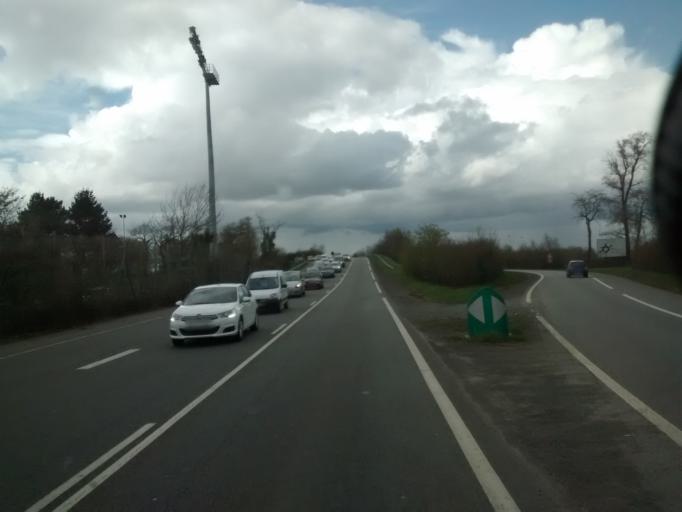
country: FR
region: Brittany
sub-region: Departement d'Ille-et-Vilaine
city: Chartres-de-Bretagne
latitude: 48.0474
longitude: -1.7048
